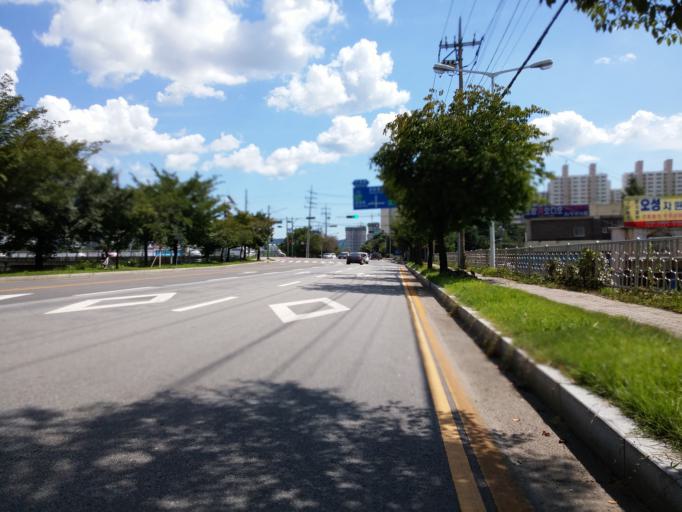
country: KR
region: Chungcheongbuk-do
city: Cheongju-si
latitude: 36.6166
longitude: 127.4931
